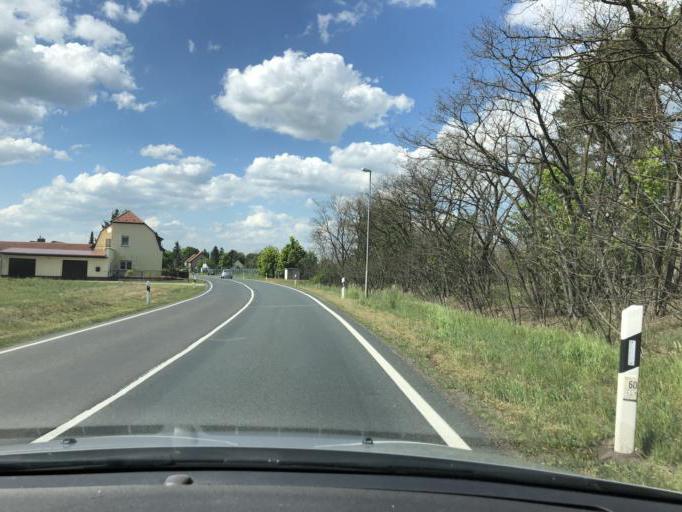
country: DE
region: Brandenburg
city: Spreenhagen
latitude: 52.3334
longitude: 13.8969
